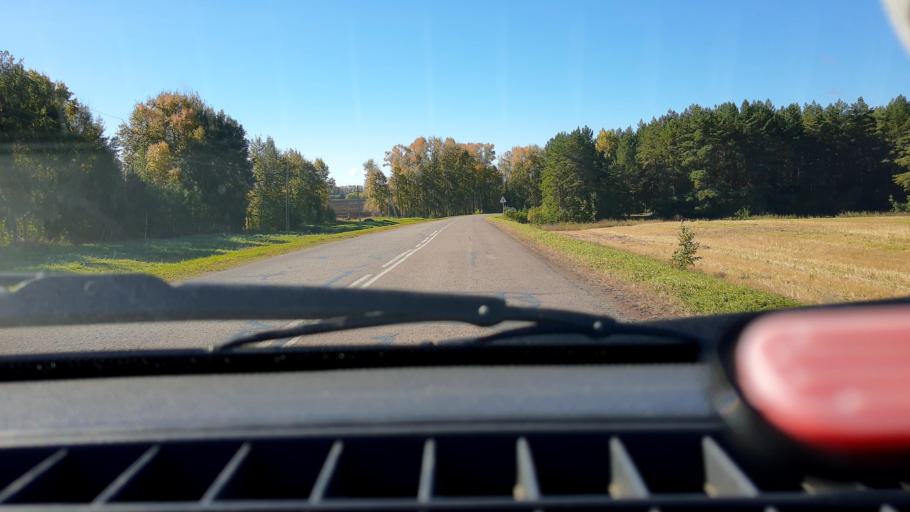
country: RU
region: Bashkortostan
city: Kushnarenkovo
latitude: 55.0649
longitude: 55.4477
